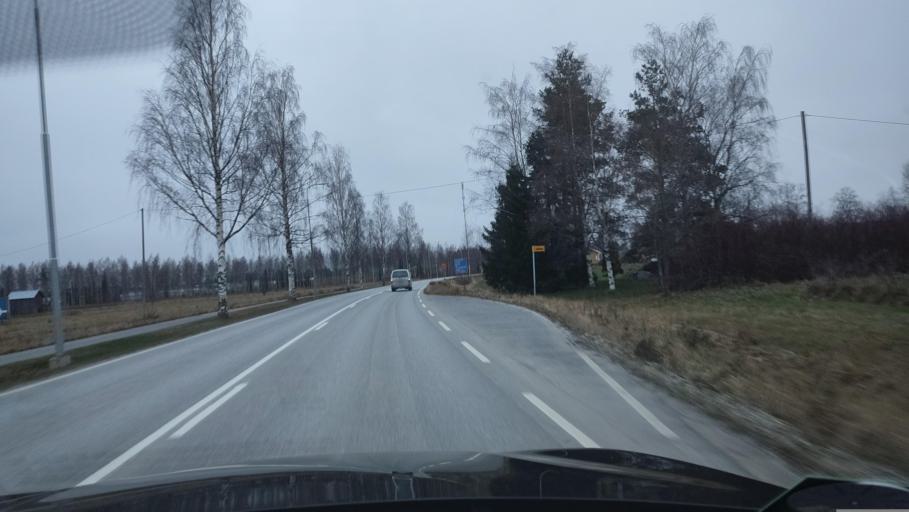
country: FI
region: Southern Ostrobothnia
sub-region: Suupohja
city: Kauhajoki
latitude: 62.4527
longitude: 22.2034
